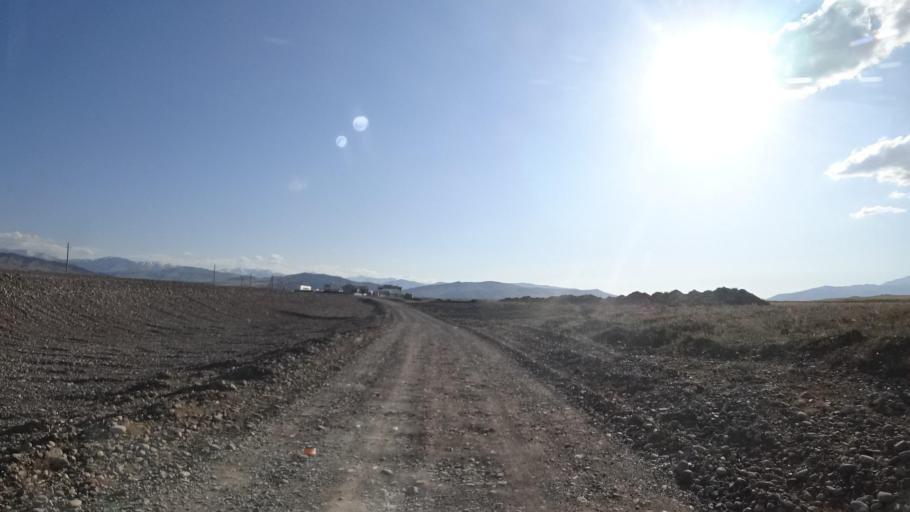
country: KZ
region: Almaty Oblysy
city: Kegen
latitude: 42.8041
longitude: 79.1843
